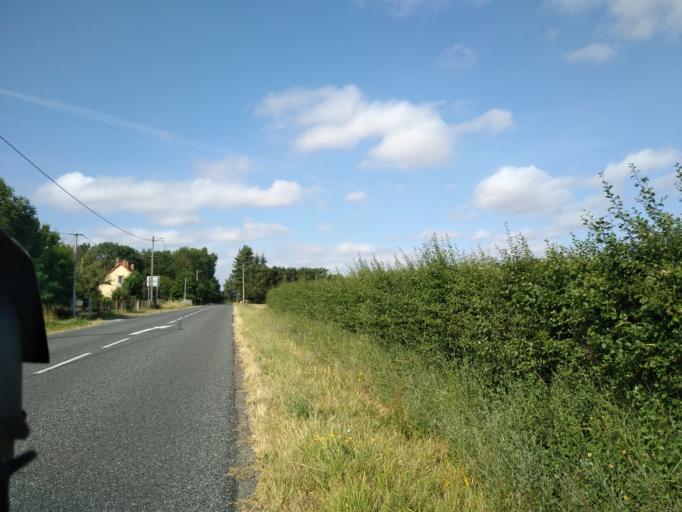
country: FR
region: Auvergne
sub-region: Departement de l'Allier
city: Saint-Pourcain-sur-Sioule
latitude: 46.2922
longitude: 3.2639
